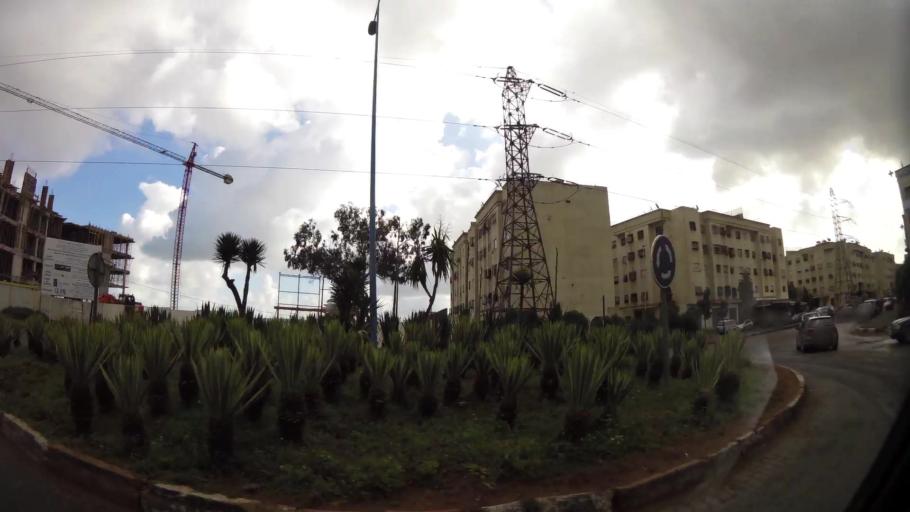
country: MA
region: Grand Casablanca
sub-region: Mediouna
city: Tit Mellil
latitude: 33.5898
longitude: -7.5267
